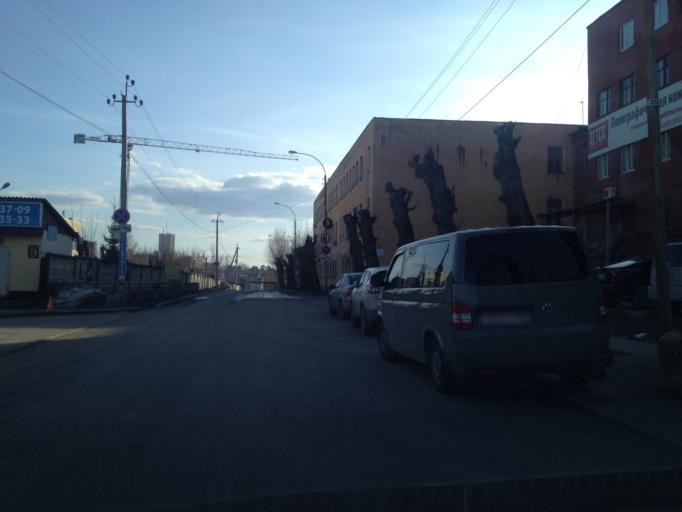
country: RU
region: Sverdlovsk
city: Sovkhoznyy
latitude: 56.8233
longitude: 60.5578
